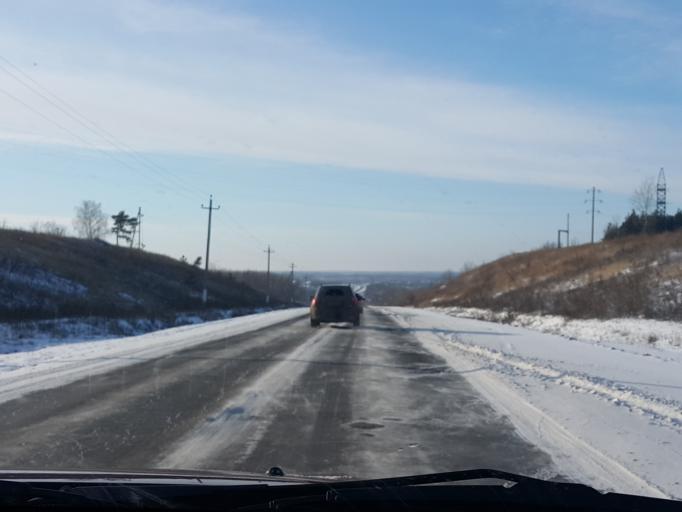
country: RU
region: Tambov
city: Znamenka
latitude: 52.4189
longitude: 41.4913
